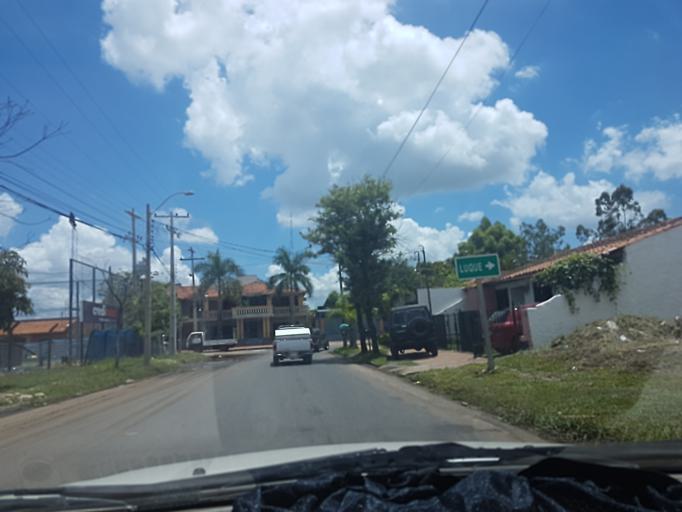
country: PY
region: Central
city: Fernando de la Mora
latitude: -25.2864
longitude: -57.5426
